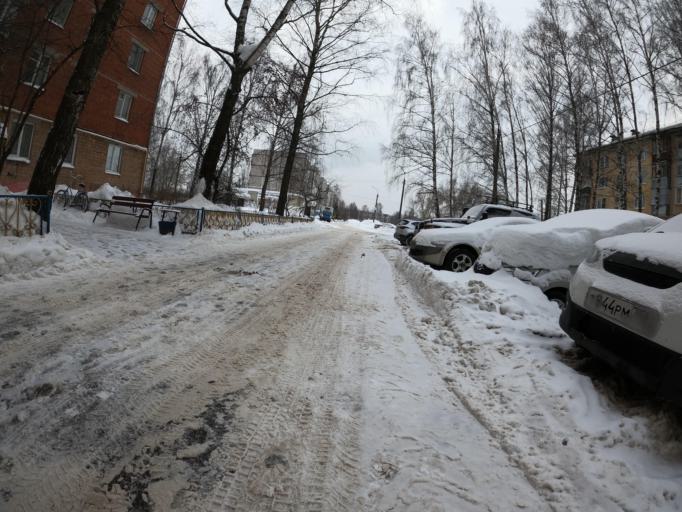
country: RU
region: Moskovskaya
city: Elektrogorsk
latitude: 55.8752
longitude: 38.7861
